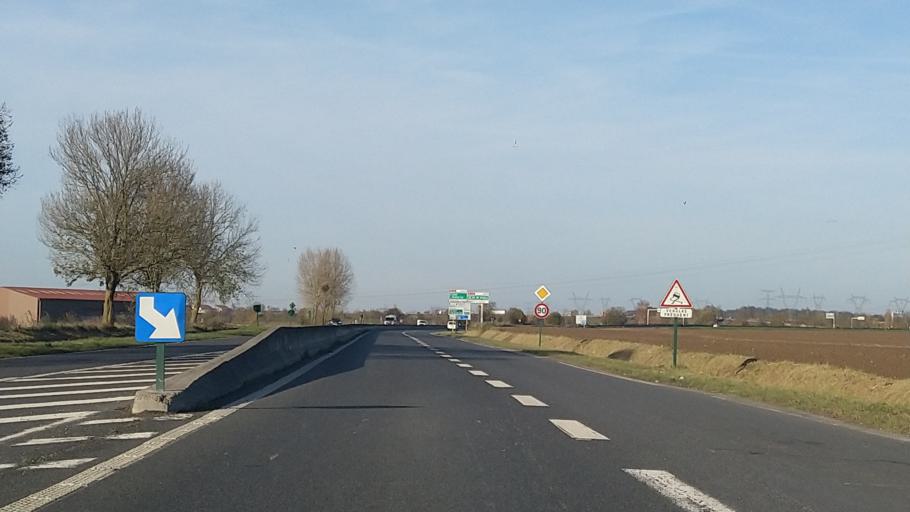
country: FR
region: Ile-de-France
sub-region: Departement du Val-d'Oise
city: Ecouen
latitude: 49.0560
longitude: 2.4021
